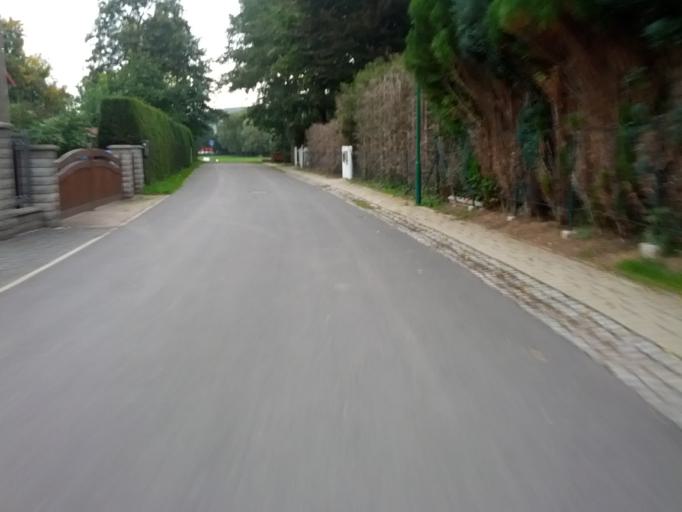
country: DE
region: Thuringia
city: Thal
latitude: 50.9441
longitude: 10.3916
